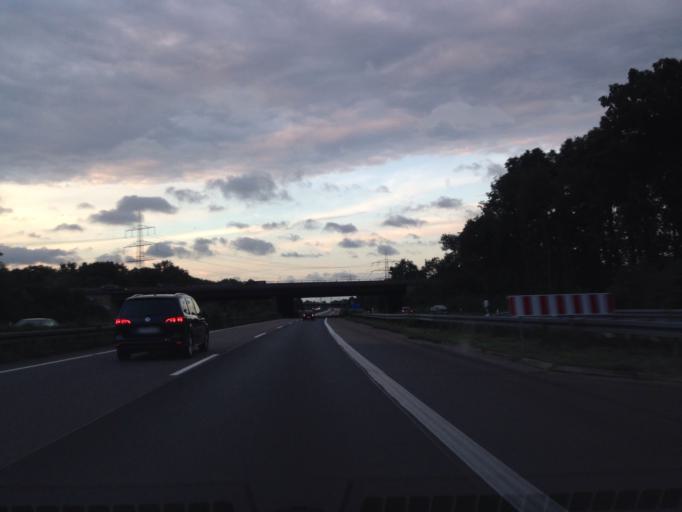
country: DE
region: North Rhine-Westphalia
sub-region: Regierungsbezirk Dusseldorf
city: Meerbusch
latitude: 51.2900
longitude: 6.6356
